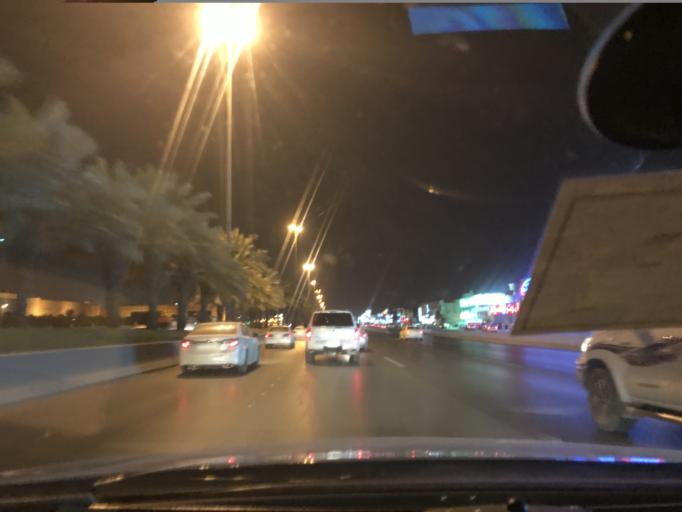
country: SA
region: Ar Riyad
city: Riyadh
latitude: 24.7434
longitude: 46.7473
